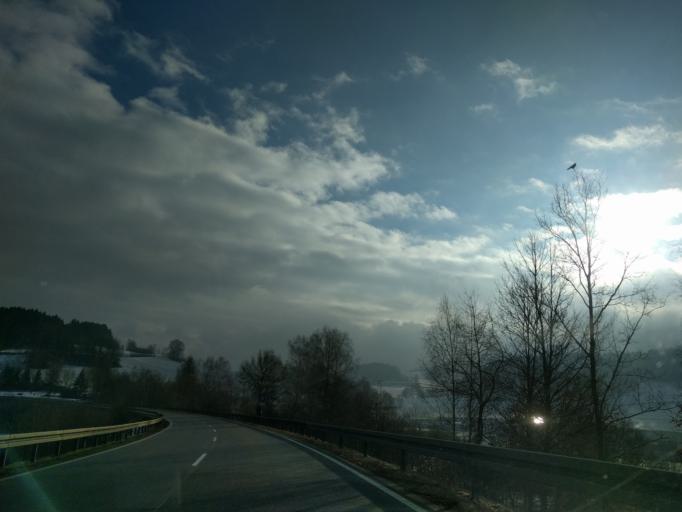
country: DE
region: Bavaria
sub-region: Lower Bavaria
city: Zwiesel
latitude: 49.0052
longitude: 13.2389
